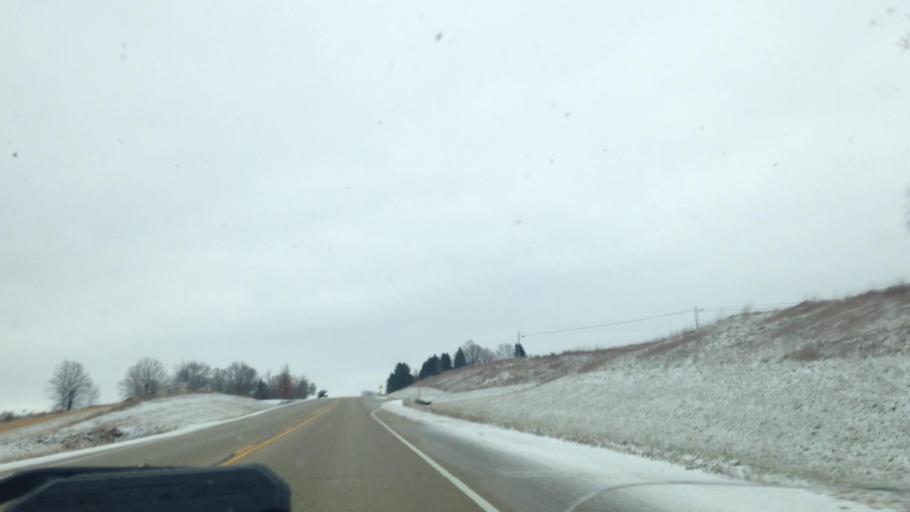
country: US
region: Wisconsin
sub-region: Dodge County
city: Horicon
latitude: 43.4716
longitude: -88.6036
